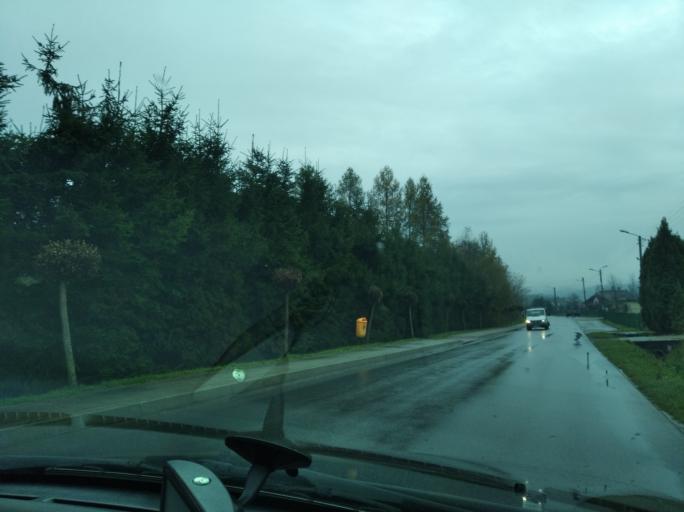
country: PL
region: Subcarpathian Voivodeship
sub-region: Powiat rzeszowski
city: Lubenia
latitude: 49.9298
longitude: 21.9227
